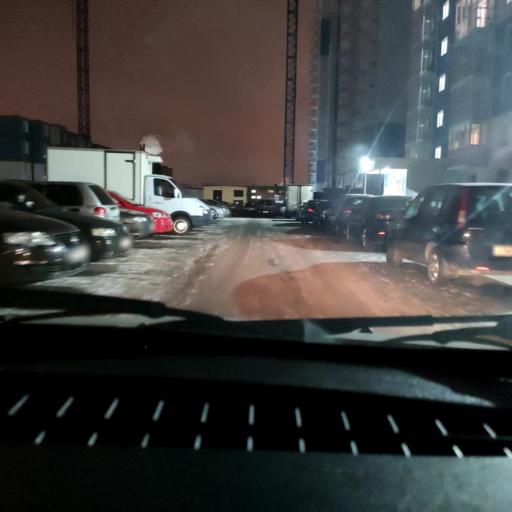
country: RU
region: Voronezj
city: Maslovka
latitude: 51.6348
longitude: 39.2989
